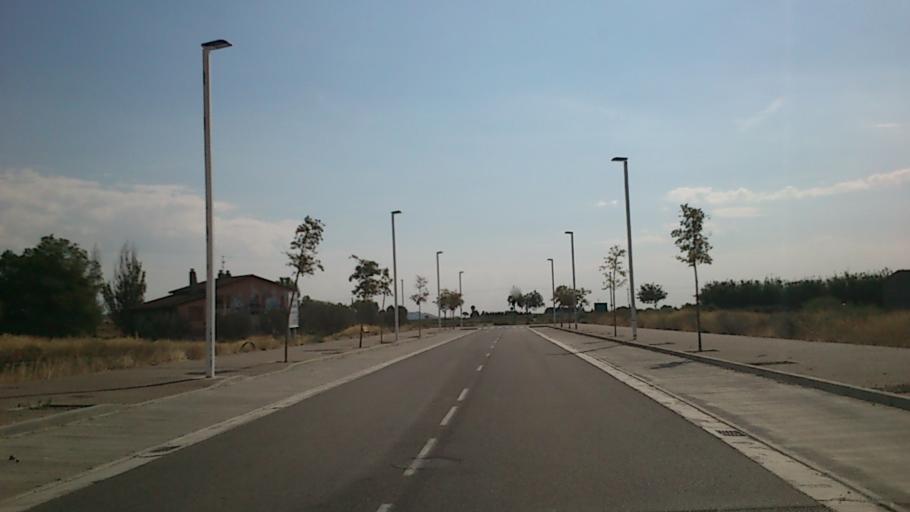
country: ES
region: Aragon
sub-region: Provincia de Zaragoza
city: Puebla de Alfinden
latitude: 41.6289
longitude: -0.7551
